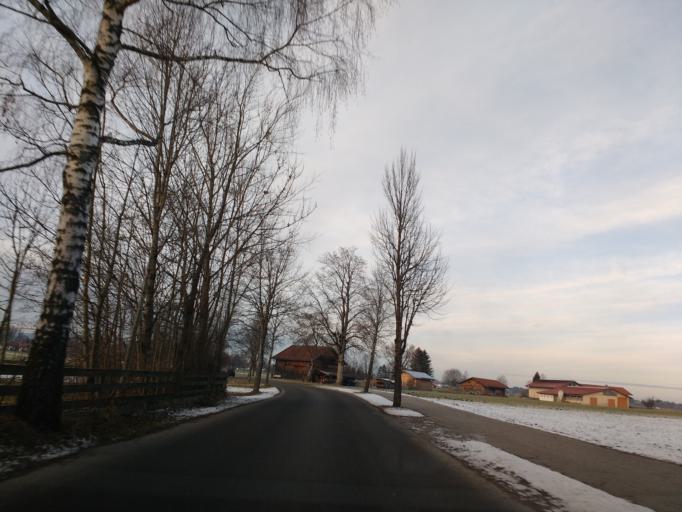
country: DE
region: Bavaria
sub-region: Swabia
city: Schwangau
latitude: 47.5691
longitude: 10.7377
